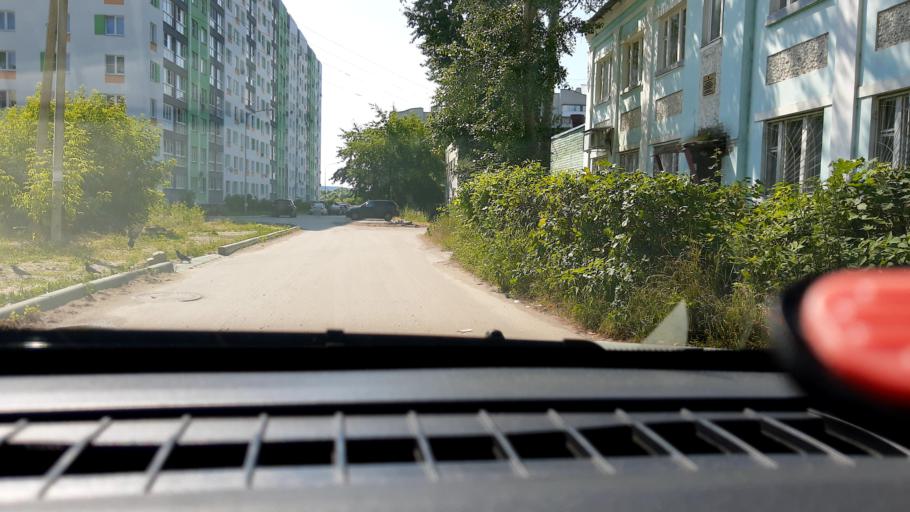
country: RU
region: Nizjnij Novgorod
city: Dzerzhinsk
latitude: 56.2320
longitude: 43.4788
